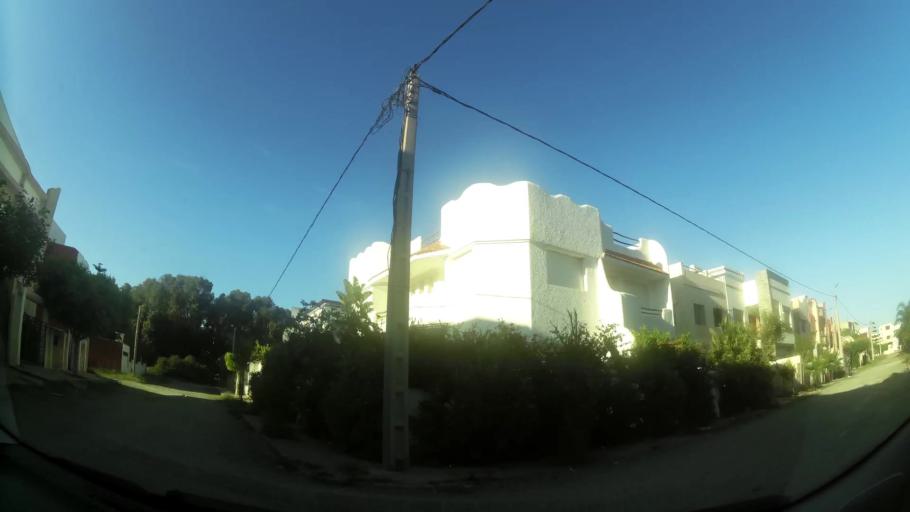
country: MA
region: Oriental
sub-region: Berkane-Taourirt
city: Madagh
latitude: 35.0889
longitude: -2.2479
